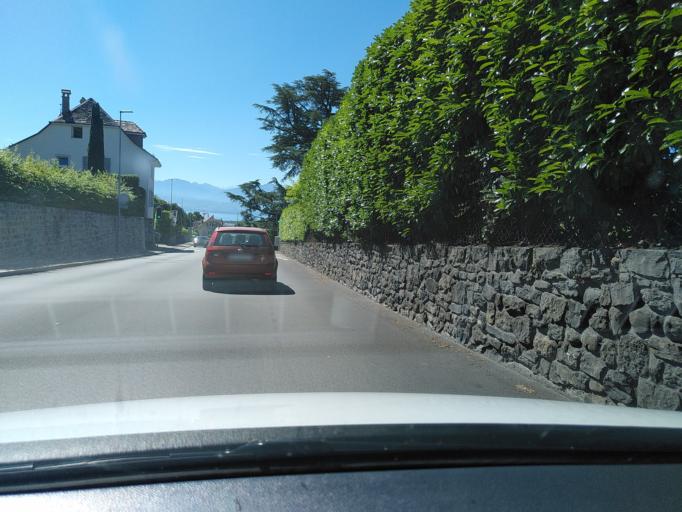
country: CH
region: Vaud
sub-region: Morges District
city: Aubonne
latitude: 46.4932
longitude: 6.3937
